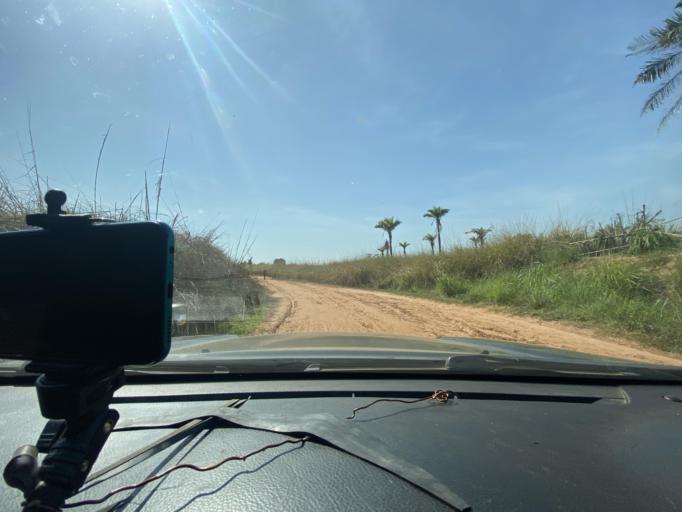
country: CD
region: Kasai-Oriental
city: Kabinda
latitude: -6.0990
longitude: 24.5437
